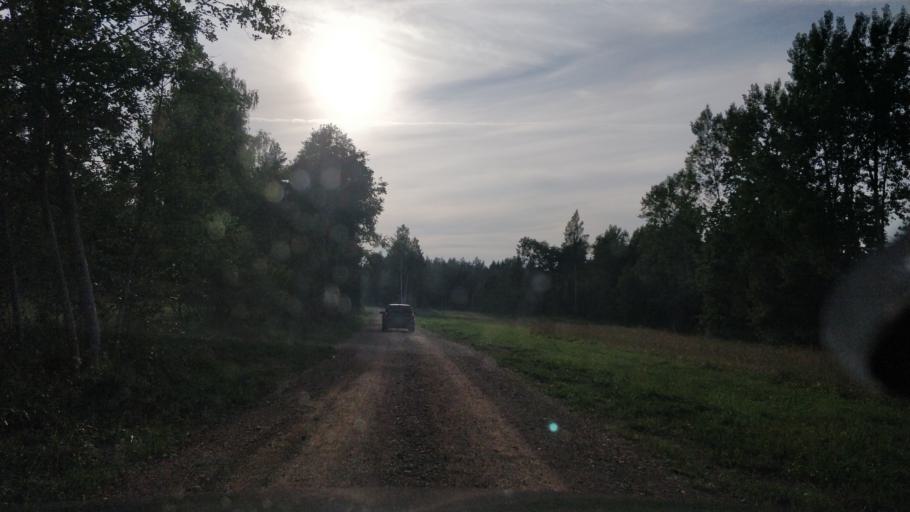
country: LV
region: Sigulda
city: Sigulda
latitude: 57.1007
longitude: 24.7891
